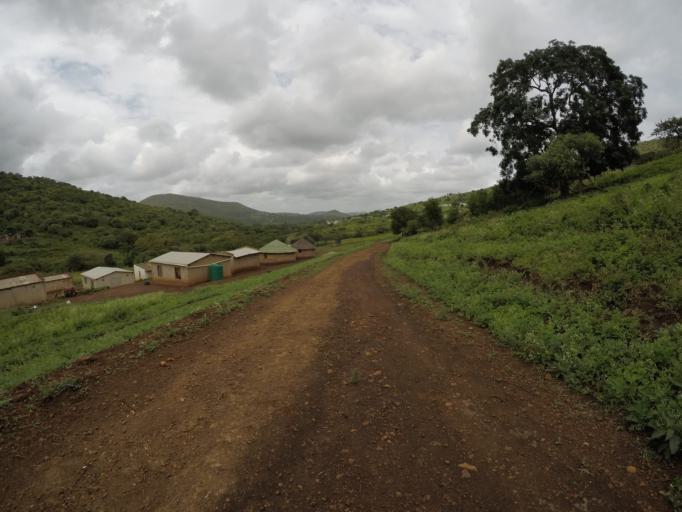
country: ZA
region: KwaZulu-Natal
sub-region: uThungulu District Municipality
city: Empangeni
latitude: -28.5814
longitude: 31.8890
